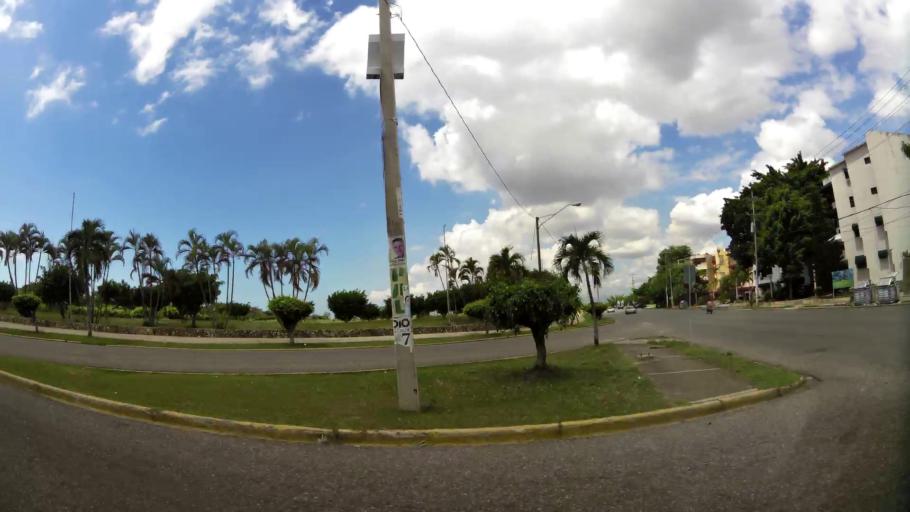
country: DO
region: Santo Domingo
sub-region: Santo Domingo
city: Santo Domingo Este
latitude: 18.4799
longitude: -69.8628
